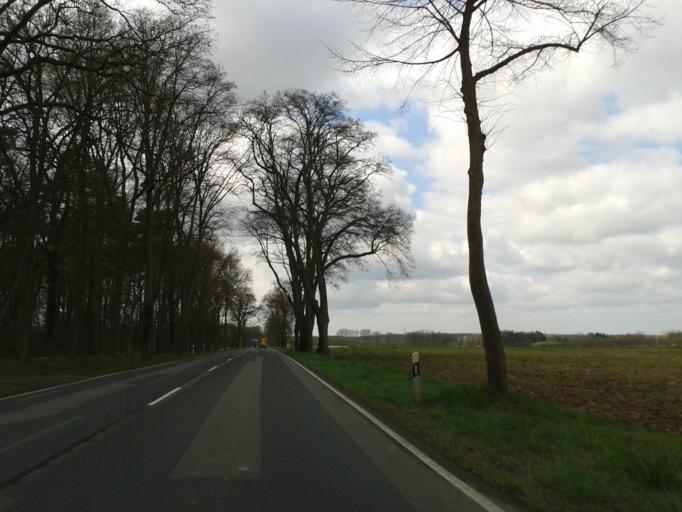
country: DE
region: Lower Saxony
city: Bergen an der Dumme
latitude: 52.8857
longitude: 10.9813
